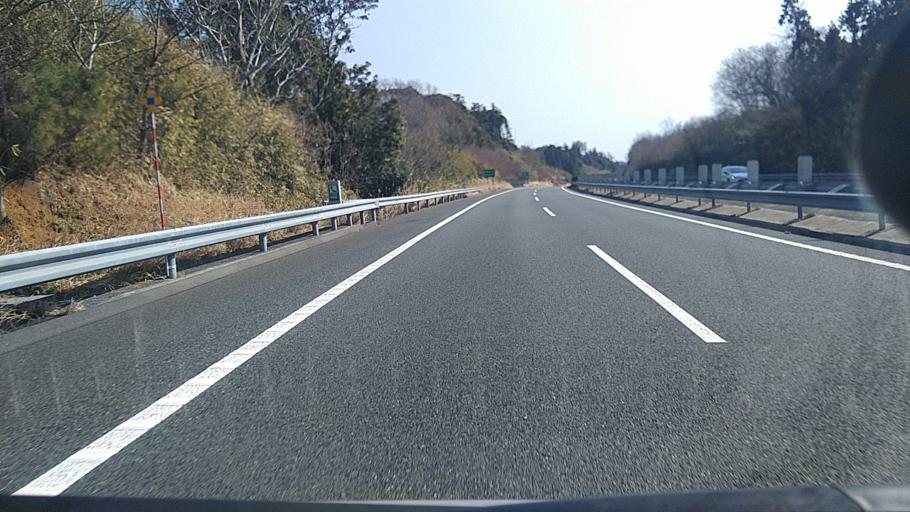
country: JP
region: Chiba
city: Kisarazu
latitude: 35.3650
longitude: 139.9970
